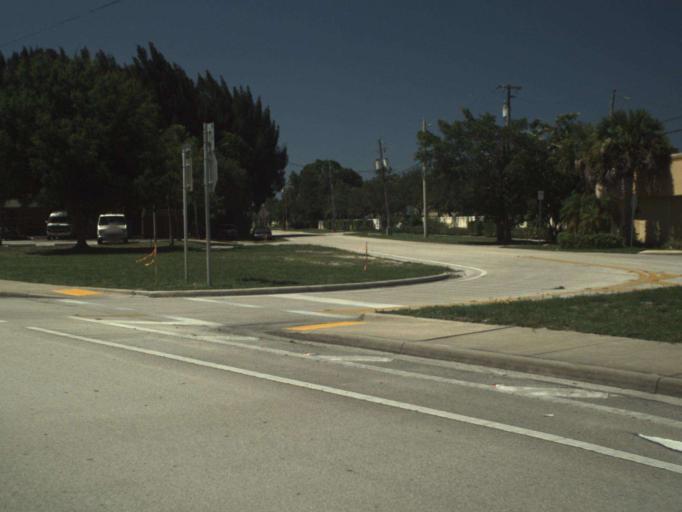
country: US
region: Florida
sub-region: Indian River County
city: Vero Beach South
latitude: 27.6118
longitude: -80.3854
